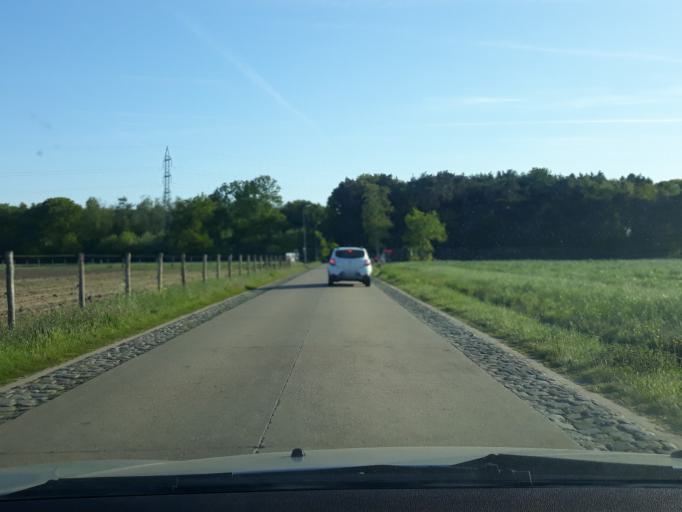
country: BE
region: Flanders
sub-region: Provincie Antwerpen
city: Vorselaar
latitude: 51.2353
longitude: 4.7602
